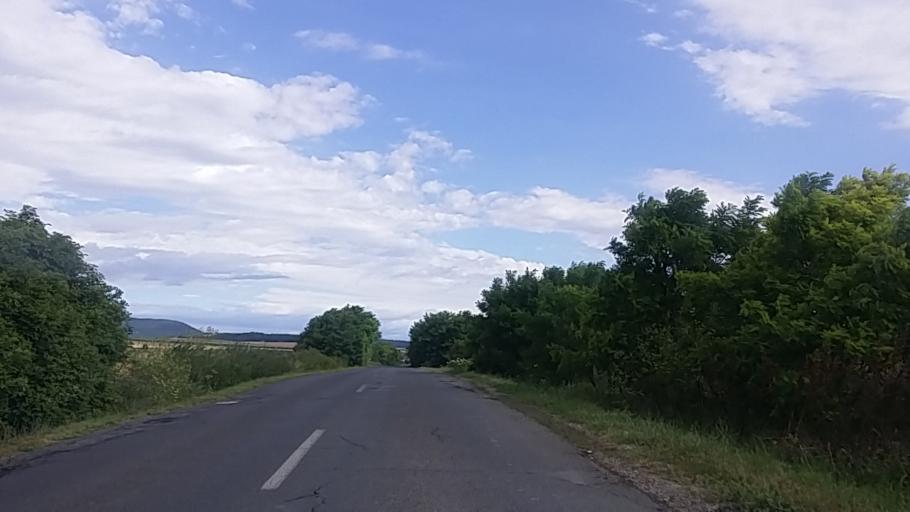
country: HU
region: Pest
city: Kosd
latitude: 47.7741
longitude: 19.2196
